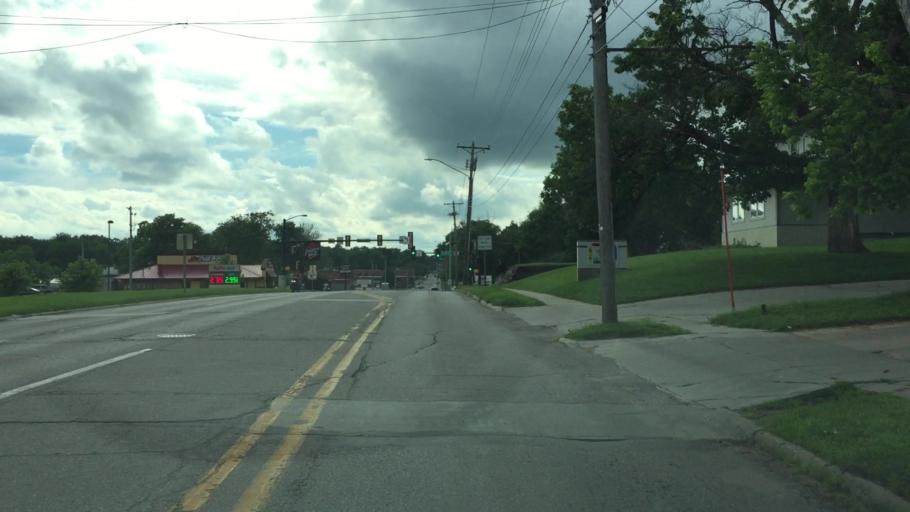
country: US
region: Iowa
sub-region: Jasper County
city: Newton
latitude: 41.6992
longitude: -93.0337
